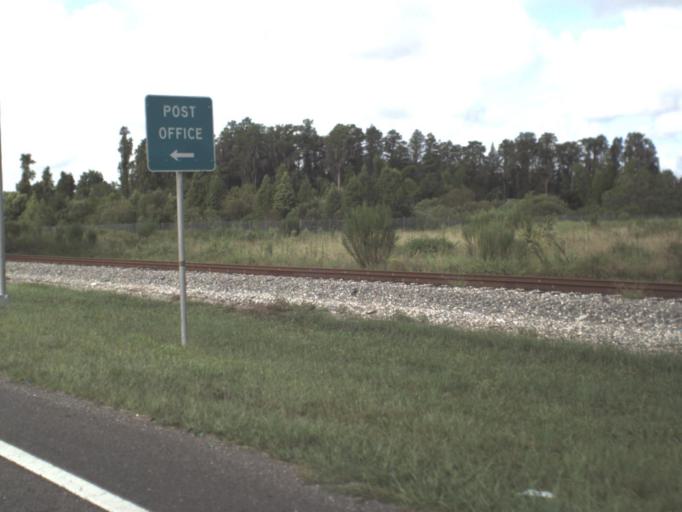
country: US
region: Florida
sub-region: Hillsborough County
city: Lutz
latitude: 28.1448
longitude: -82.4624
